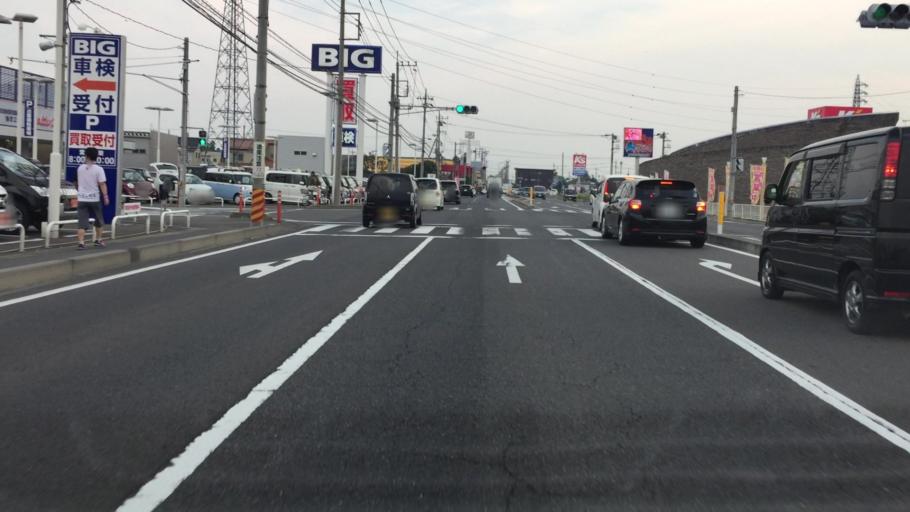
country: JP
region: Tochigi
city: Tochigi
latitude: 36.3497
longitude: 139.7083
